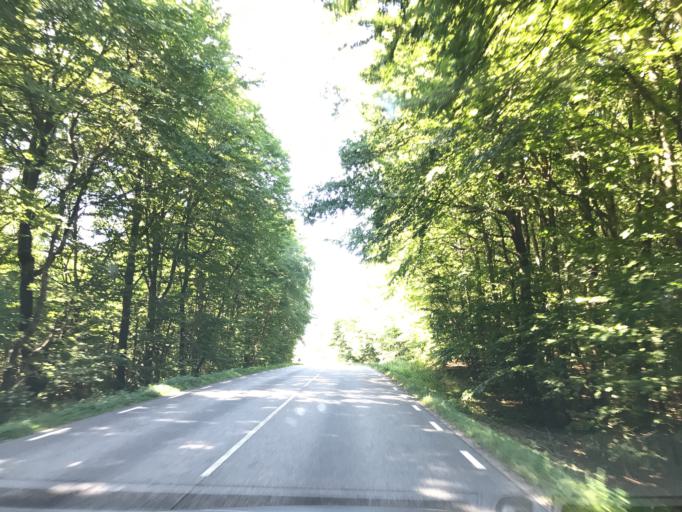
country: SE
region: Skane
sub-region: Tomelilla Kommun
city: Tomelilla
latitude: 55.6539
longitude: 13.9342
